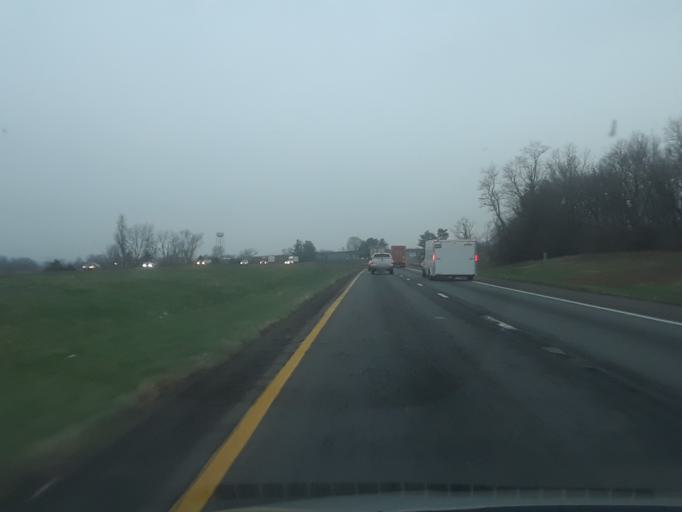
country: US
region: Virginia
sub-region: Shenandoah County
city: Mount Jackson
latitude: 38.7773
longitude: -78.6178
